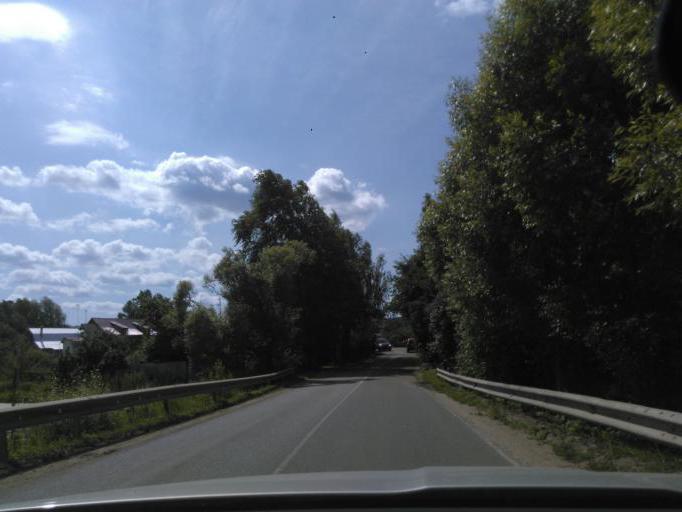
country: RU
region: Moskovskaya
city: Solnechnogorsk
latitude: 56.1644
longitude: 36.9765
